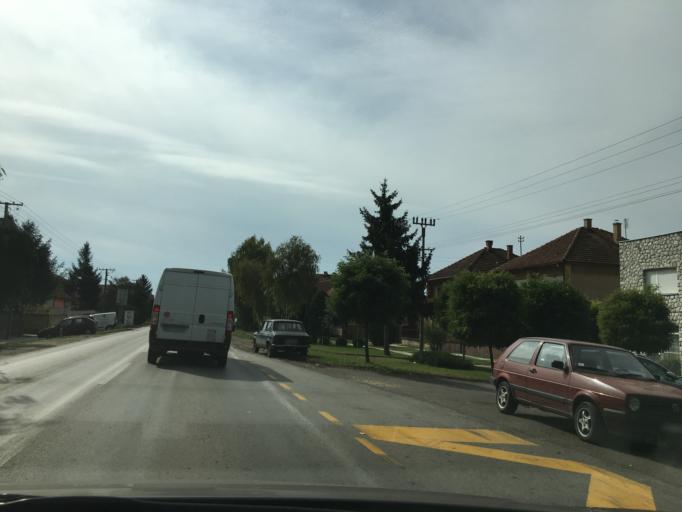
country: RS
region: Autonomna Pokrajina Vojvodina
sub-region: Juznobacki Okrug
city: Temerin
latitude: 45.3903
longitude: 19.8805
